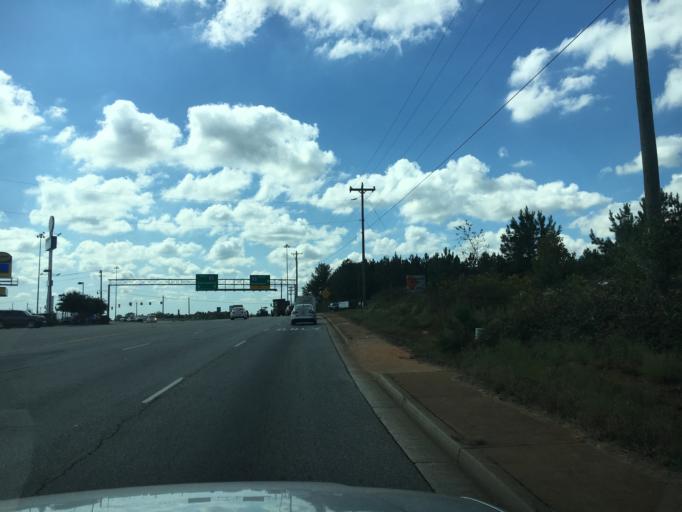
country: US
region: South Carolina
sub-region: Greenville County
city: Greer
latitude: 34.8747
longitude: -82.2252
